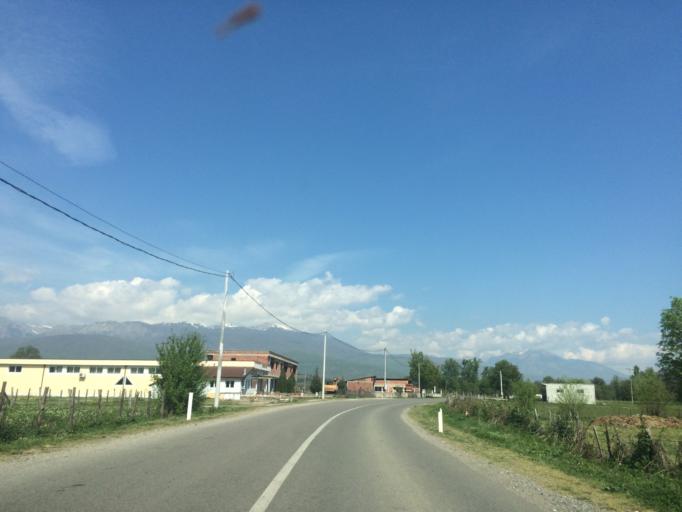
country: XK
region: Gjakova
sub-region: Komuna e Junikut
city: Junik
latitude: 42.3930
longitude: 20.2984
